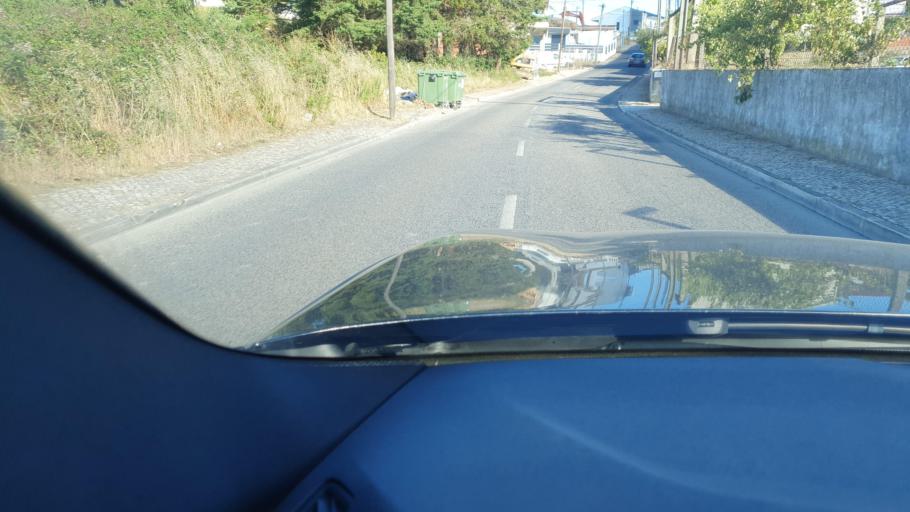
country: PT
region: Lisbon
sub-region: Sintra
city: Belas
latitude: 38.7956
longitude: -9.2514
